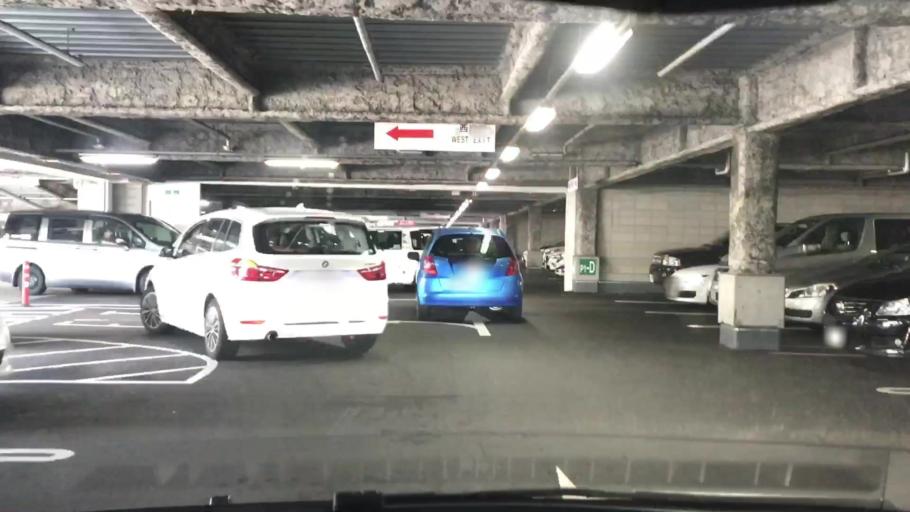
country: JP
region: Hyogo
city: Amagasaki
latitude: 34.7414
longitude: 135.4436
